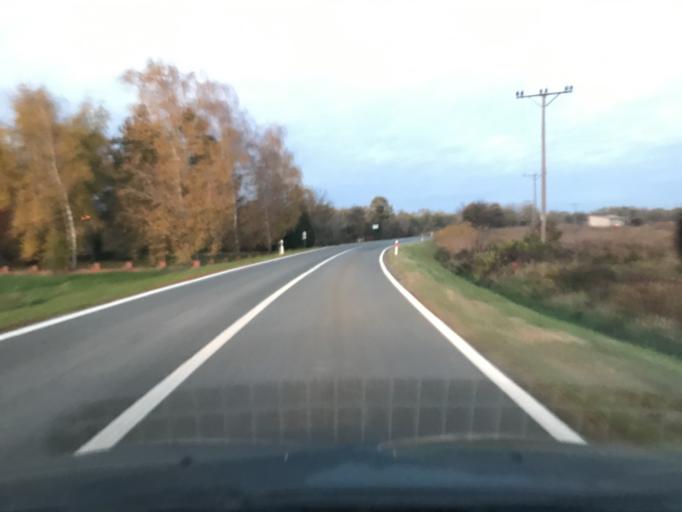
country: HR
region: Sisacko-Moslavacka
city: Novska
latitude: 45.2736
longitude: 16.9098
